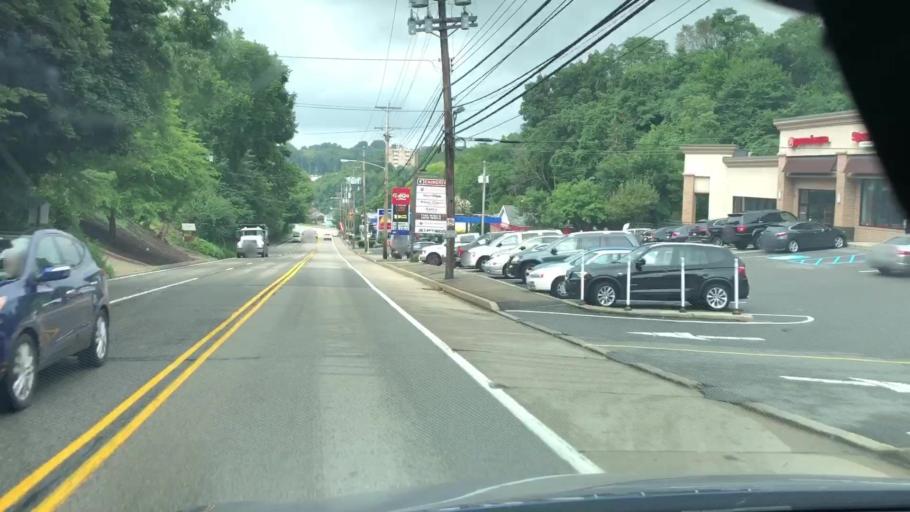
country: US
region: Pennsylvania
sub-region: Allegheny County
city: Green Tree
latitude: 40.3911
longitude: -80.0596
